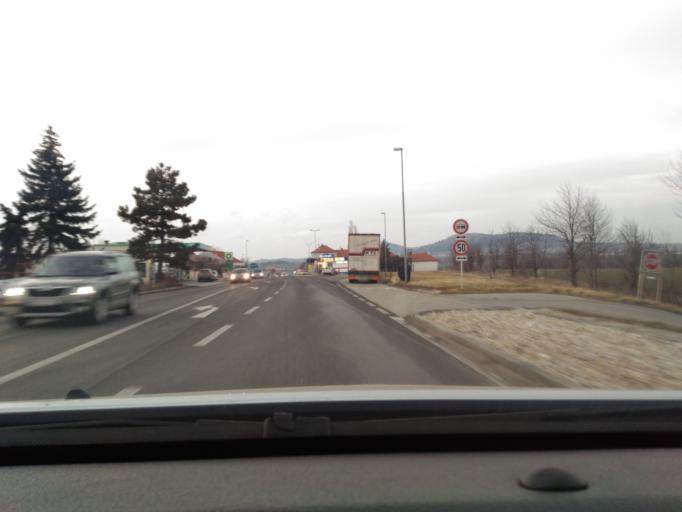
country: AT
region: Lower Austria
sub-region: Politischer Bezirk Mistelbach
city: Drasenhofen
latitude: 48.7767
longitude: 16.6412
